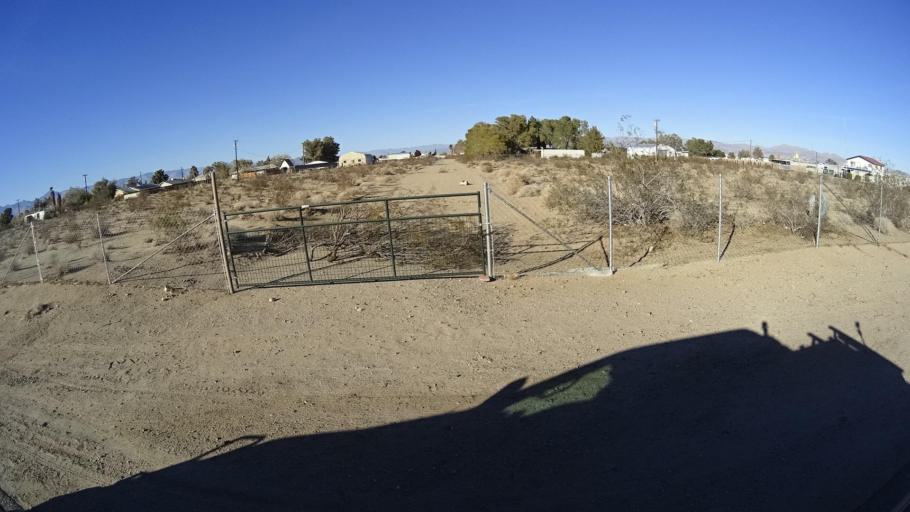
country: US
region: California
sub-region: Kern County
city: Ridgecrest
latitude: 35.6444
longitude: -117.6978
